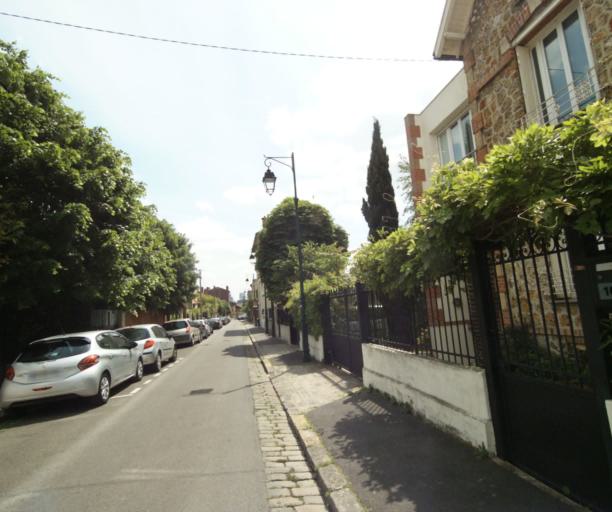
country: FR
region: Ile-de-France
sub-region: Departement des Hauts-de-Seine
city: La Garenne-Colombes
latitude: 48.9155
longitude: 2.2350
